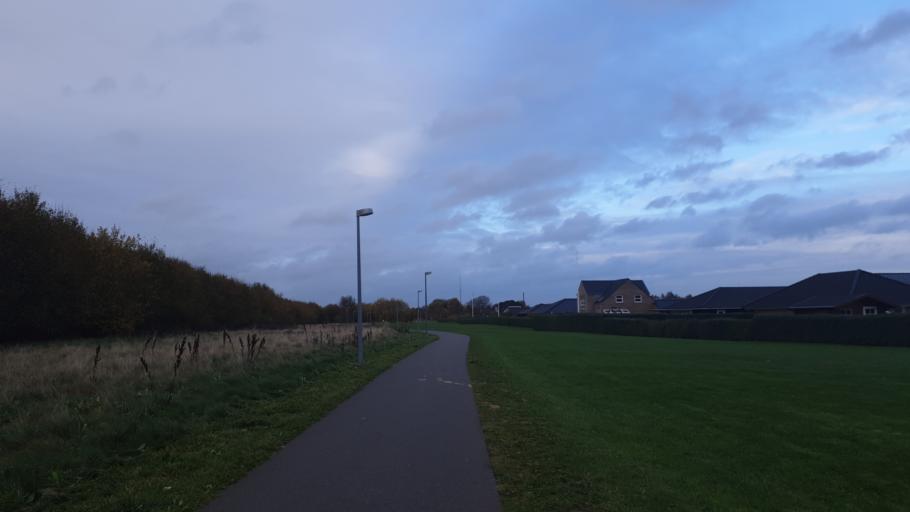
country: DK
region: Central Jutland
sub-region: Hedensted Kommune
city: Hedensted
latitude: 55.7856
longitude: 9.6919
